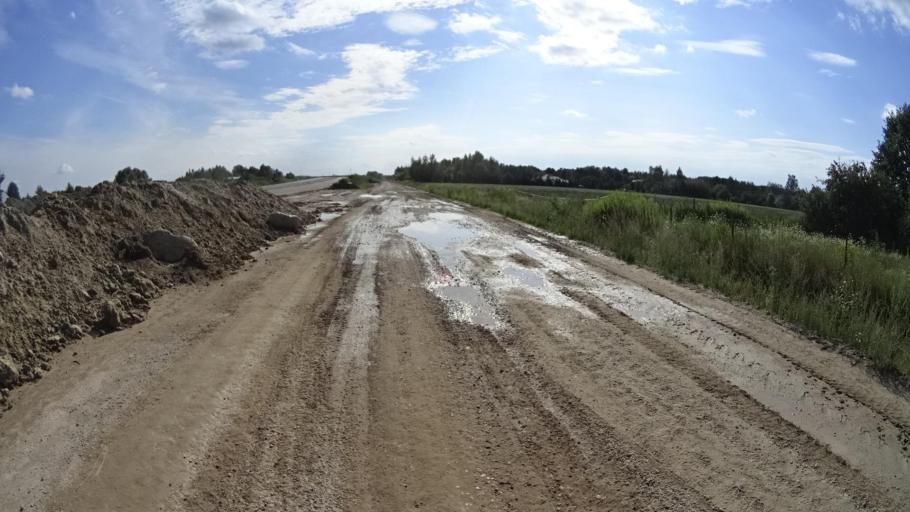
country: PL
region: Masovian Voivodeship
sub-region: Powiat piaseczynski
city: Lesznowola
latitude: 52.0589
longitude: 20.9300
